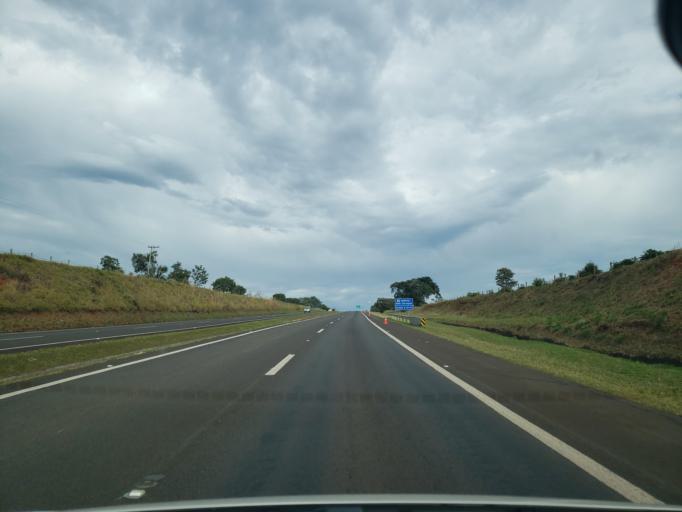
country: BR
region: Sao Paulo
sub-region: Dois Corregos
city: Dois Corregos
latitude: -22.2585
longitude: -48.3682
